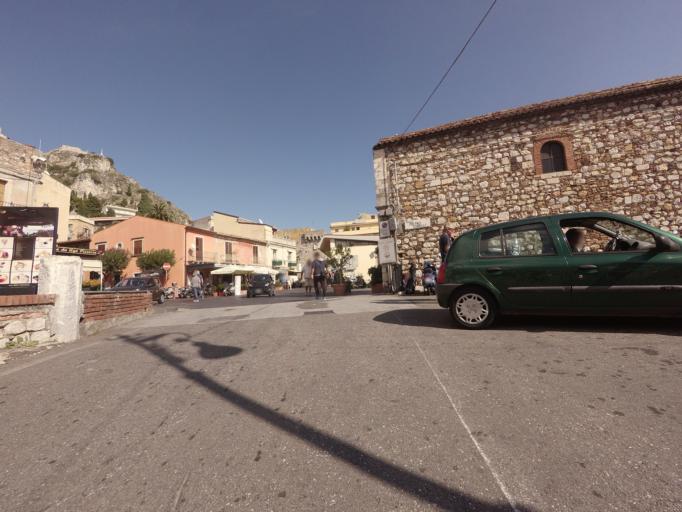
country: IT
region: Sicily
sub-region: Messina
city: Taormina
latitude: 37.8511
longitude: 15.2810
